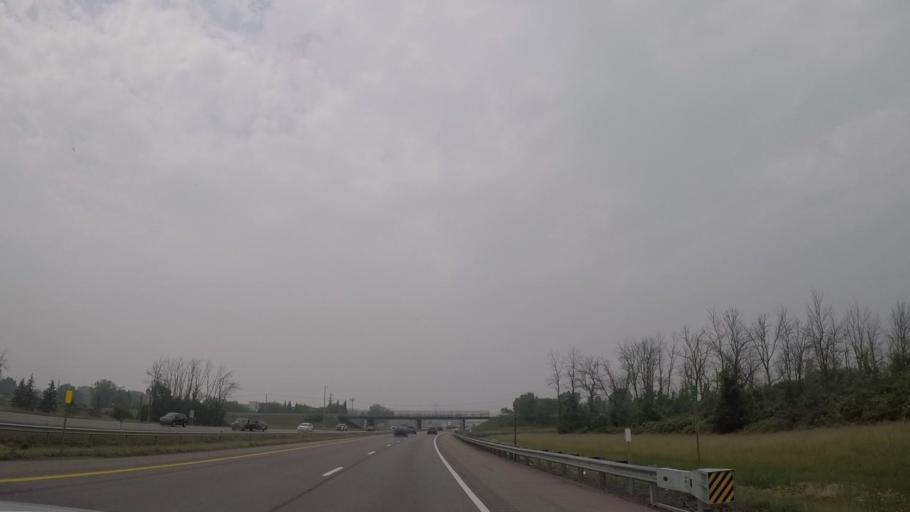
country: US
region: New York
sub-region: Erie County
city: Grandyle Village
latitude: 43.0466
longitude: -78.9901
